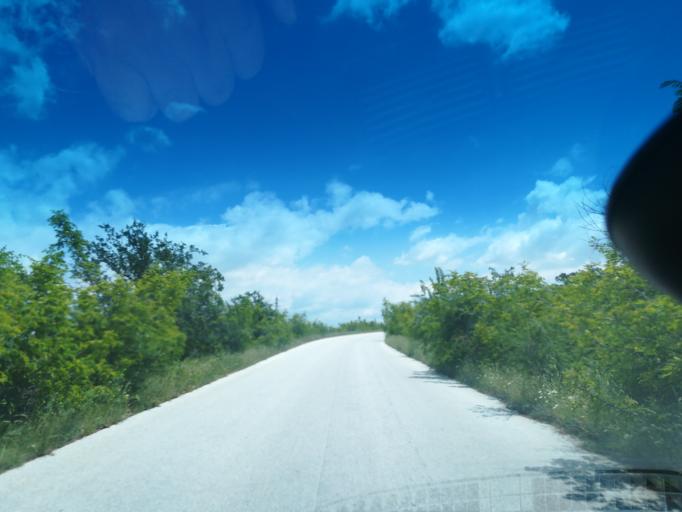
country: BG
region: Khaskovo
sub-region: Obshtina Mineralni Bani
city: Mineralni Bani
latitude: 41.9777
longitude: 25.2547
